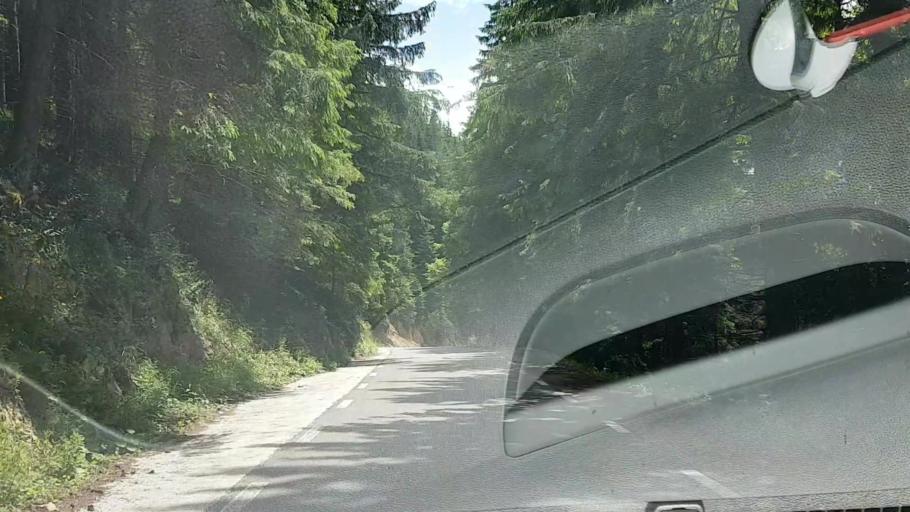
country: RO
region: Suceava
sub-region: Municipiul Campulung Moldovenesc
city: Campulung Moldovenesc
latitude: 47.4489
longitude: 25.5526
